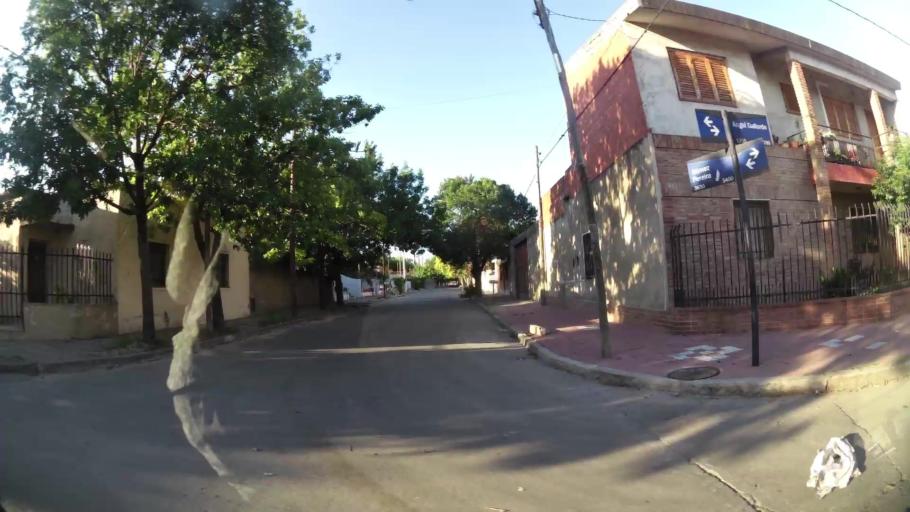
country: AR
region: Cordoba
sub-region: Departamento de Capital
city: Cordoba
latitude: -31.3739
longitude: -64.1976
